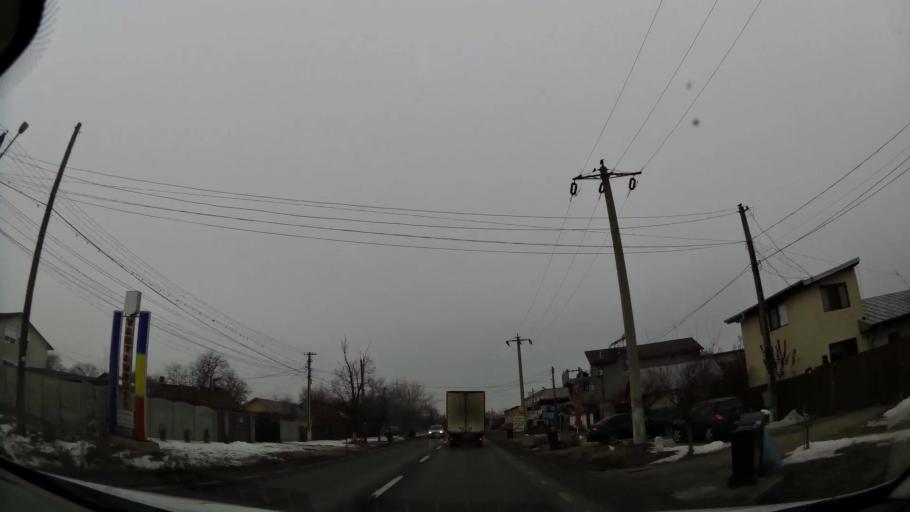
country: RO
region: Dambovita
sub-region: Comuna Racari
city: Racari
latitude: 44.6204
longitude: 25.7539
